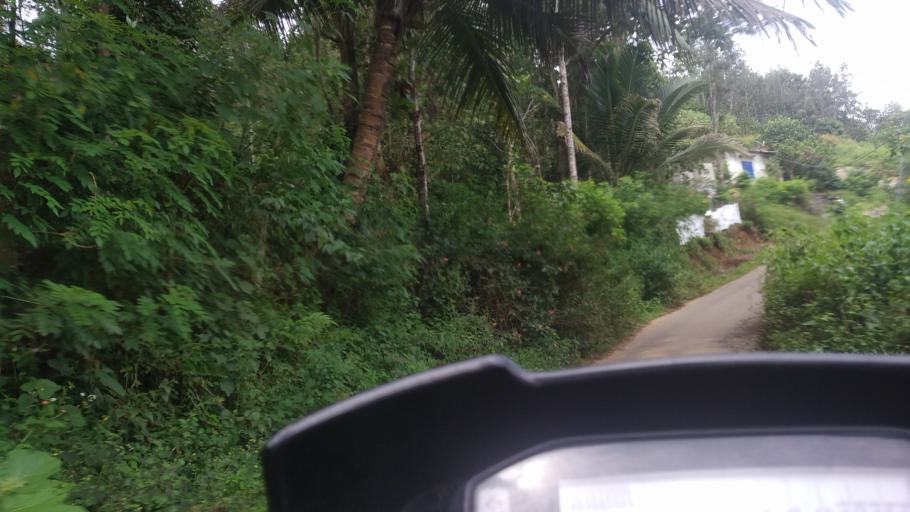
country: IN
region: Tamil Nadu
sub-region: Theni
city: Gudalur
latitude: 9.5769
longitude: 77.0773
